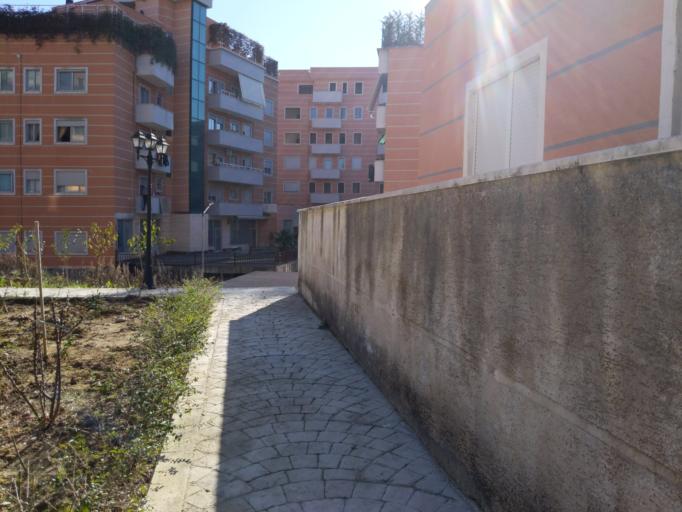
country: AL
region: Tirane
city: Tirana
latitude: 41.3089
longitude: 19.8045
